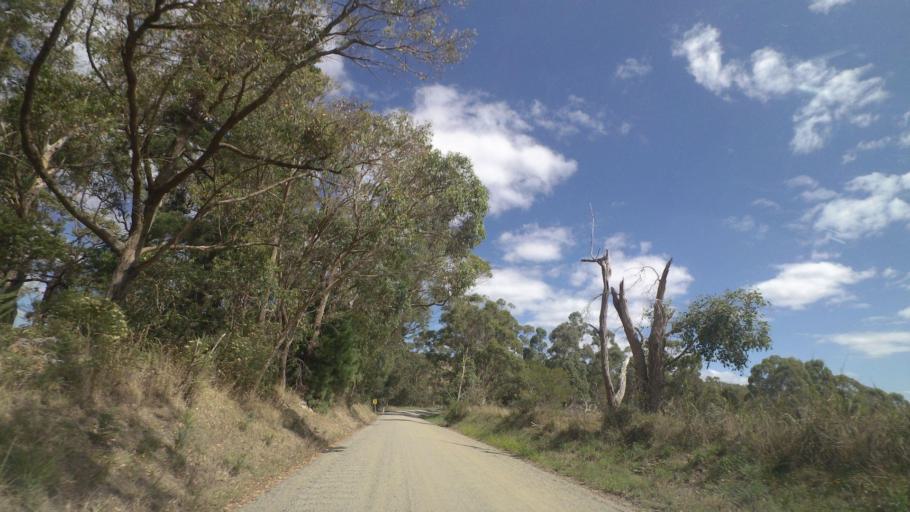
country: AU
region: Victoria
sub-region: Cardinia
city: Bunyip
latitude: -38.3225
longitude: 145.7267
